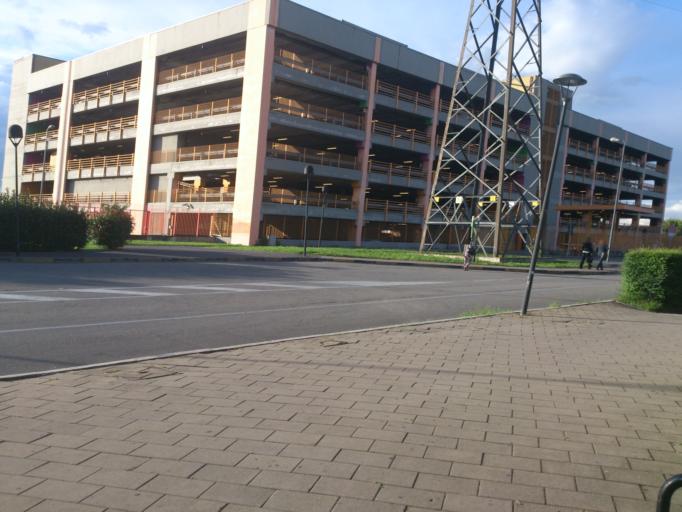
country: IT
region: Lombardy
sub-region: Citta metropolitana di Milano
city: San Donato Milanese
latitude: 45.4288
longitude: 9.2577
